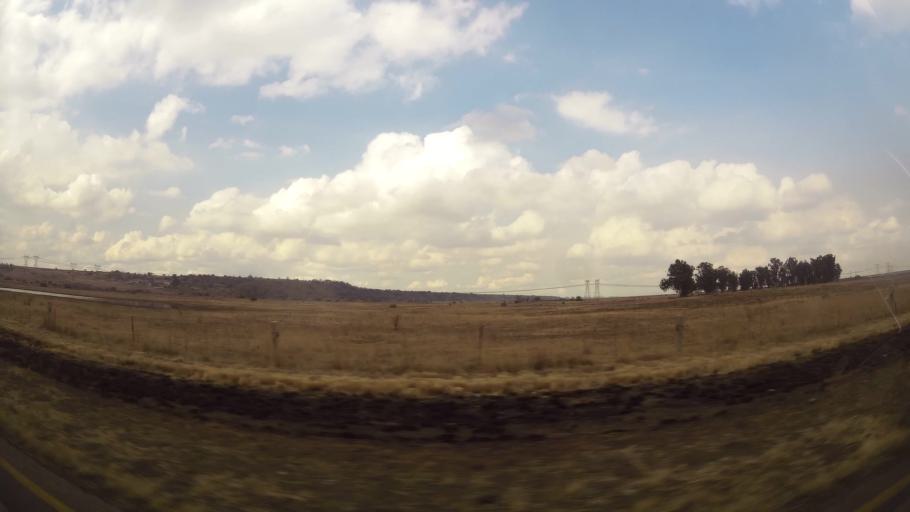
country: ZA
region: Orange Free State
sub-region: Fezile Dabi District Municipality
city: Sasolburg
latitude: -26.8102
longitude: 27.9107
